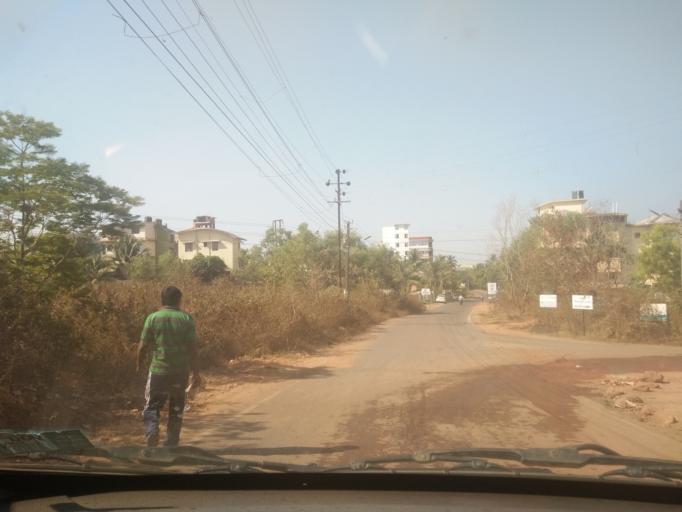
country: IN
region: Goa
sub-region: South Goa
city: Chicalim
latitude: 15.3927
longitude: 73.8627
